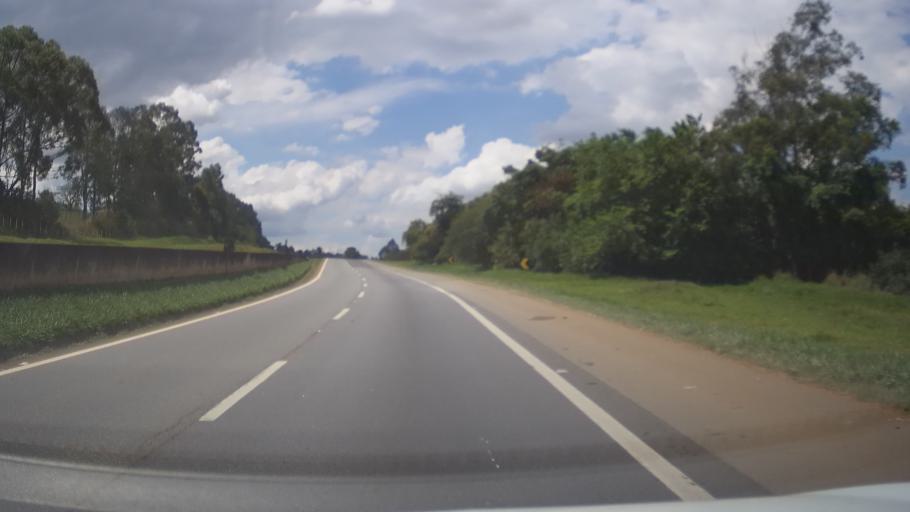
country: BR
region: Minas Gerais
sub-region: Nepomuceno
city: Nepomuceno
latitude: -21.2544
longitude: -45.1388
